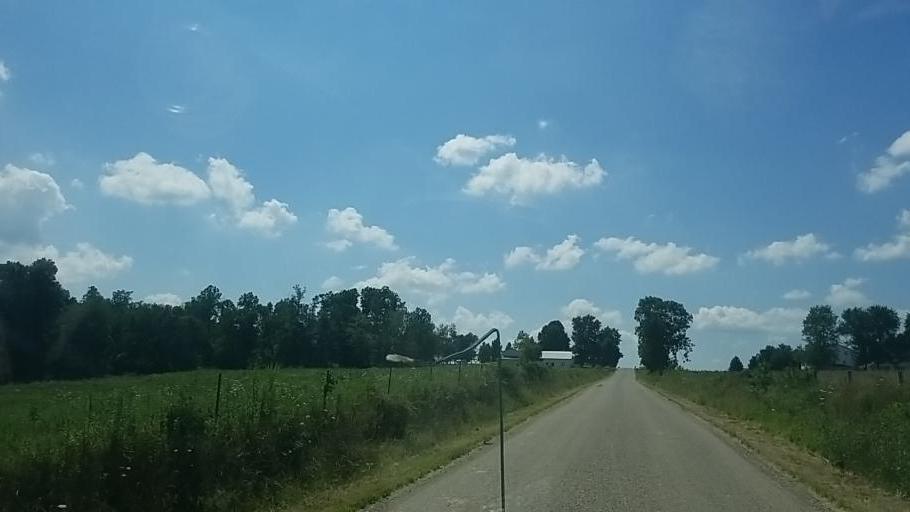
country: US
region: Ohio
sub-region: Wayne County
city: Apple Creek
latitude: 40.6826
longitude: -81.7390
